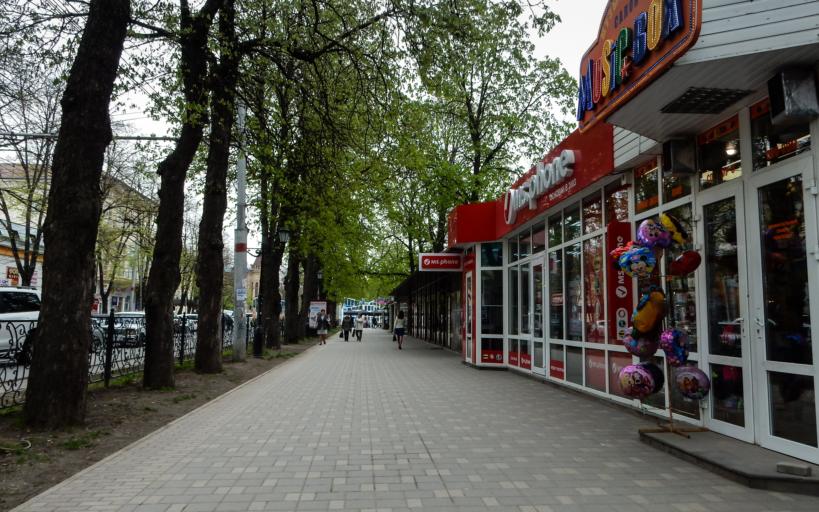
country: RU
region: Stavropol'skiy
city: Pyatigorsk
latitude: 44.0359
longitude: 43.0650
